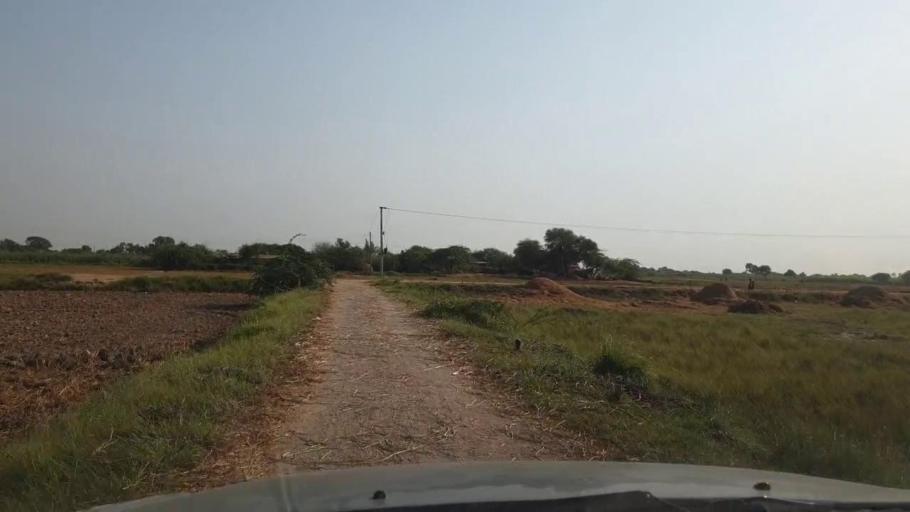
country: PK
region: Sindh
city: Bulri
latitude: 24.9160
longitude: 68.3134
